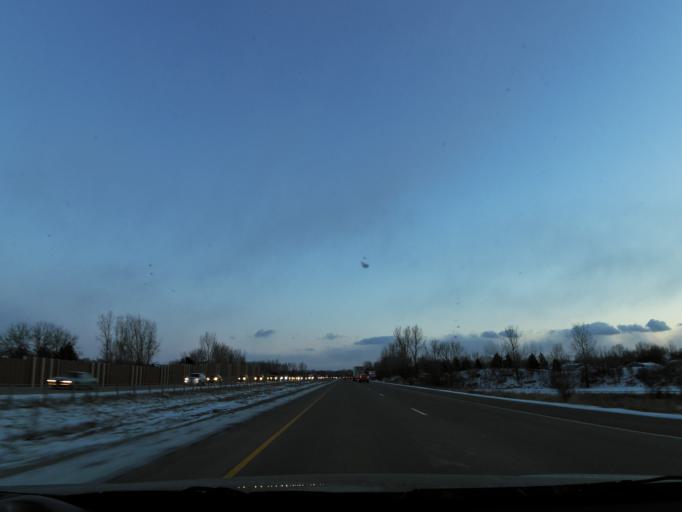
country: US
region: Minnesota
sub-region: Ramsey County
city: North Saint Paul
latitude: 45.0138
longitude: -92.9587
